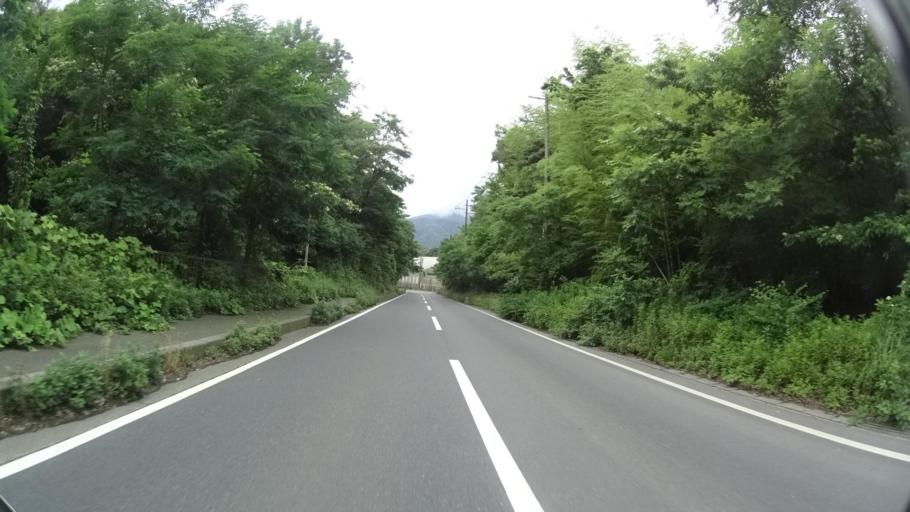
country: JP
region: Kyoto
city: Maizuru
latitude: 35.4982
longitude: 135.3894
